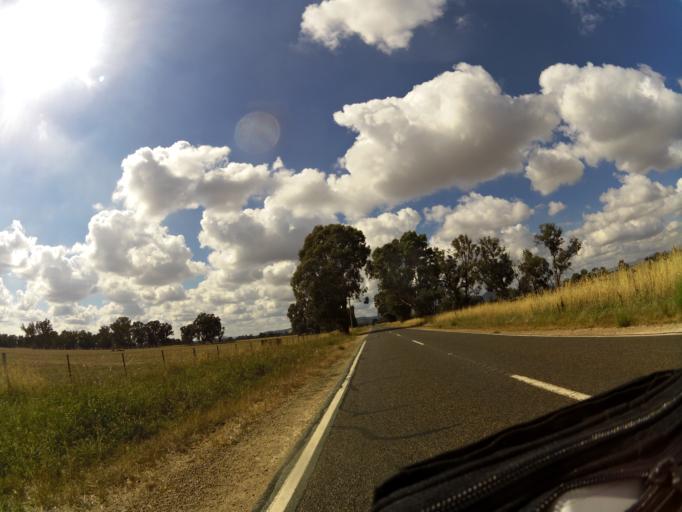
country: AU
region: Victoria
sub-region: Benalla
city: Benalla
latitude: -36.6480
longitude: 146.0542
